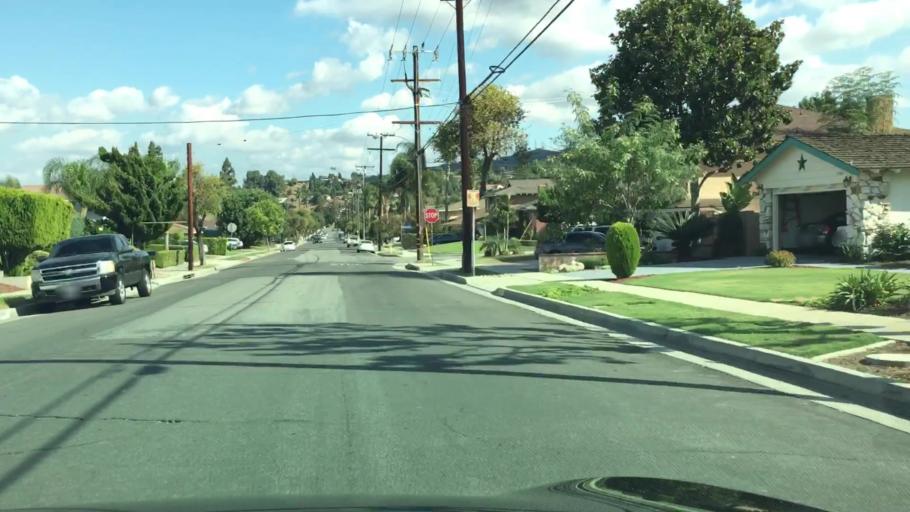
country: US
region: California
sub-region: Los Angeles County
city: Hacienda Heights
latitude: 33.9918
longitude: -117.9767
